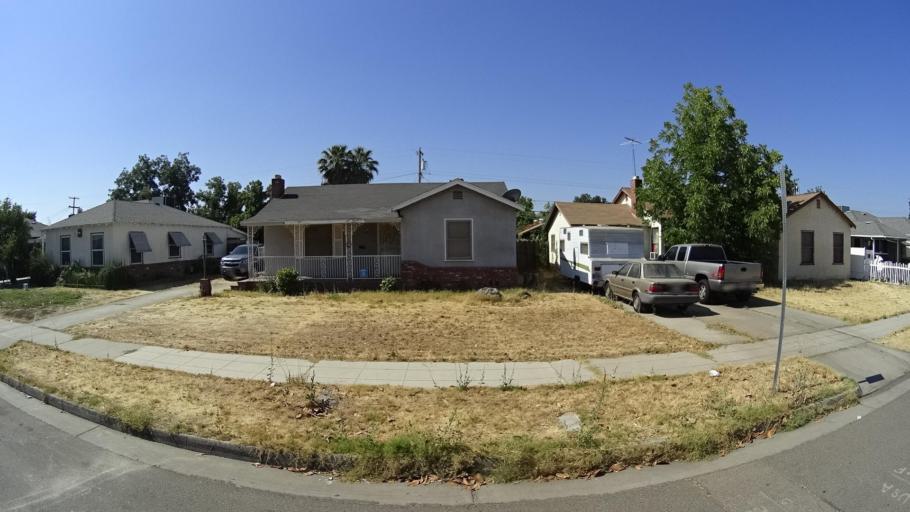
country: US
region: California
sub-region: Fresno County
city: Fresno
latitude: 36.7768
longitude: -119.7759
